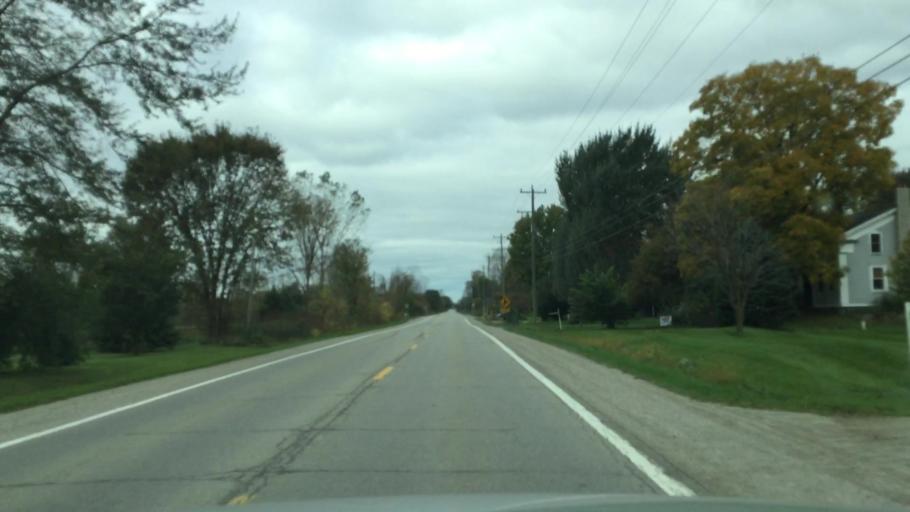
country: US
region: Michigan
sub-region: Macomb County
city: Armada
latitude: 42.8058
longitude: -82.9205
